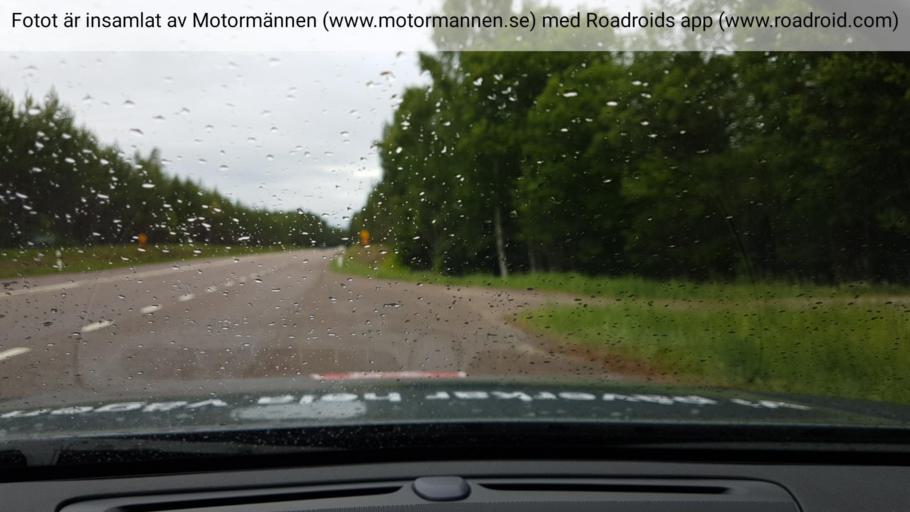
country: SE
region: Uppsala
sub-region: Alvkarleby Kommun
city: AElvkarleby
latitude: 60.6039
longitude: 17.4462
